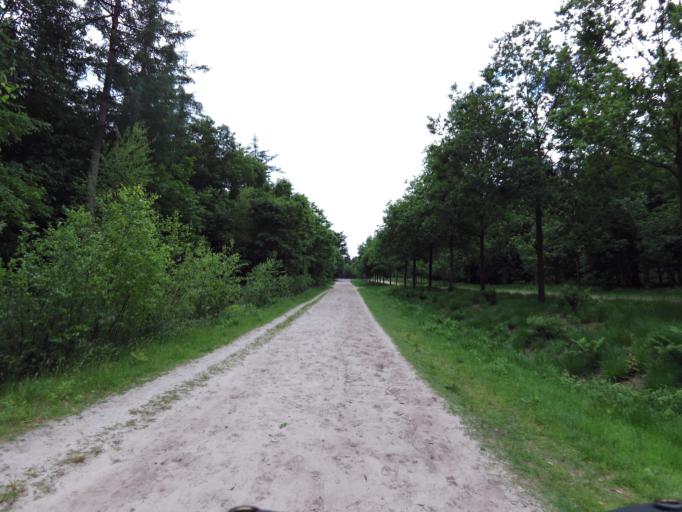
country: NL
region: North Brabant
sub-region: Gemeente Breda
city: Breda
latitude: 51.5601
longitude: 4.7766
